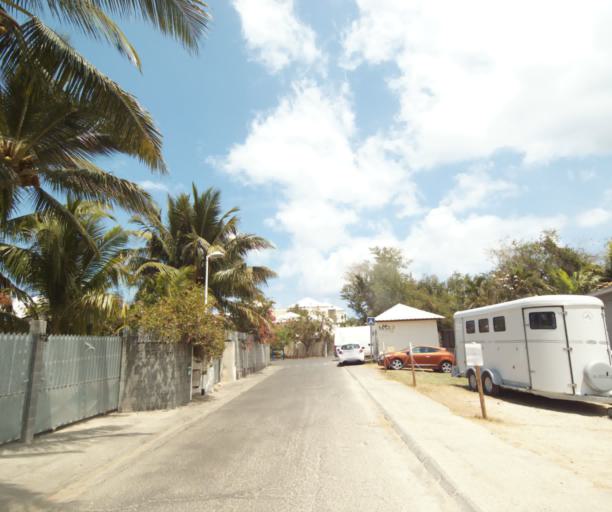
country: RE
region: Reunion
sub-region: Reunion
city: Saint-Paul
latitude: -21.0735
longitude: 55.2250
